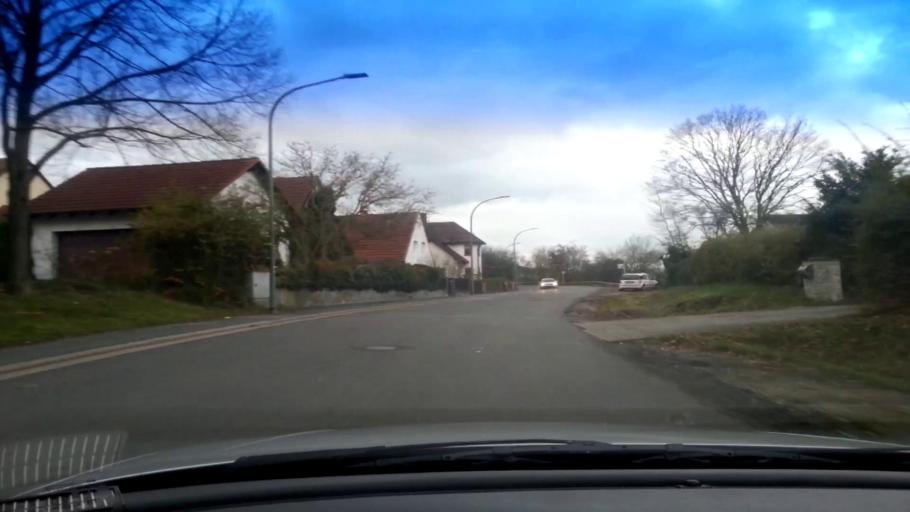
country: DE
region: Bavaria
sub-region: Upper Franconia
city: Stegaurach
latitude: 49.8772
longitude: 10.8622
